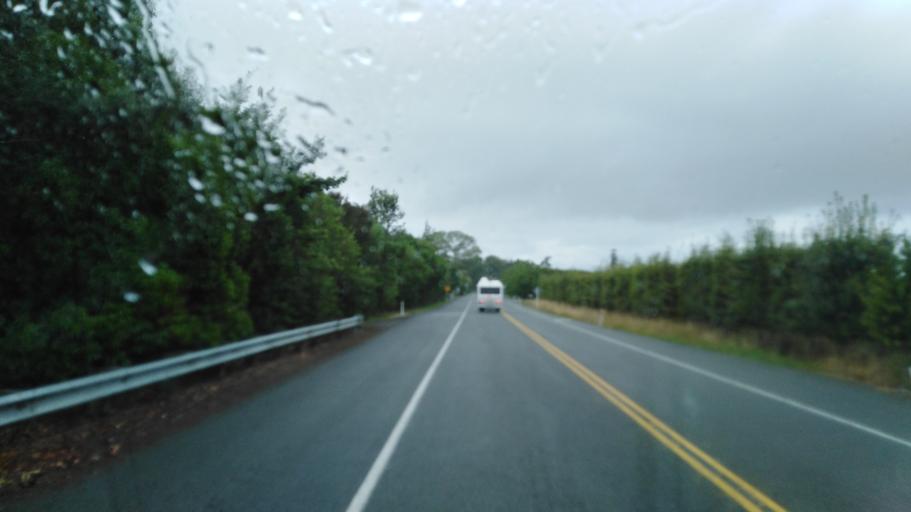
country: NZ
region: Marlborough
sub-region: Marlborough District
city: Blenheim
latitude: -41.4586
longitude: 173.9488
